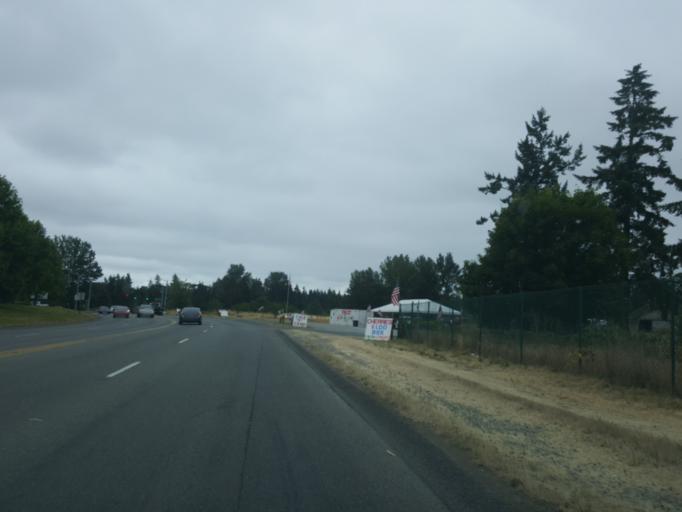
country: US
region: Washington
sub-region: Pierce County
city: Parkland
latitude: 47.1462
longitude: -122.4606
